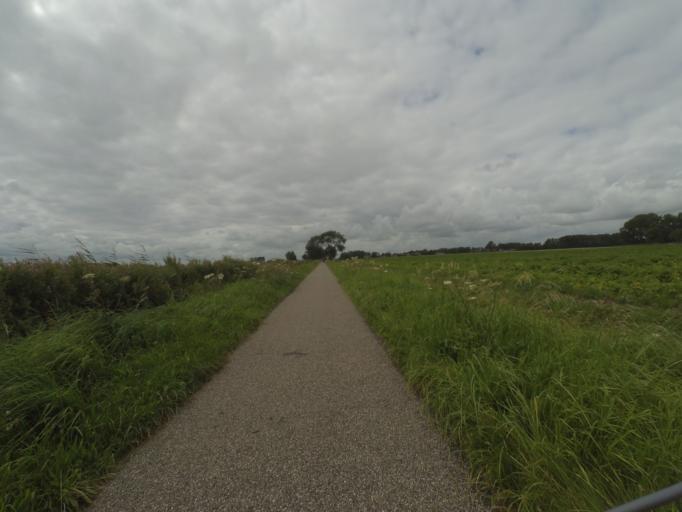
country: NL
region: Friesland
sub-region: Gemeente Kollumerland en Nieuwkruisland
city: Kollum
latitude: 53.3161
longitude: 6.1498
